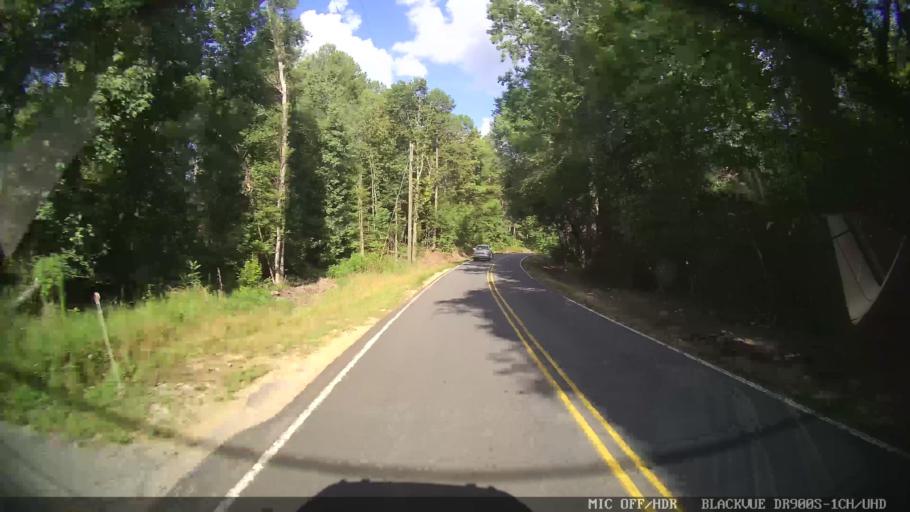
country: US
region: Georgia
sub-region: Floyd County
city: Lindale
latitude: 34.1910
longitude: -85.0590
